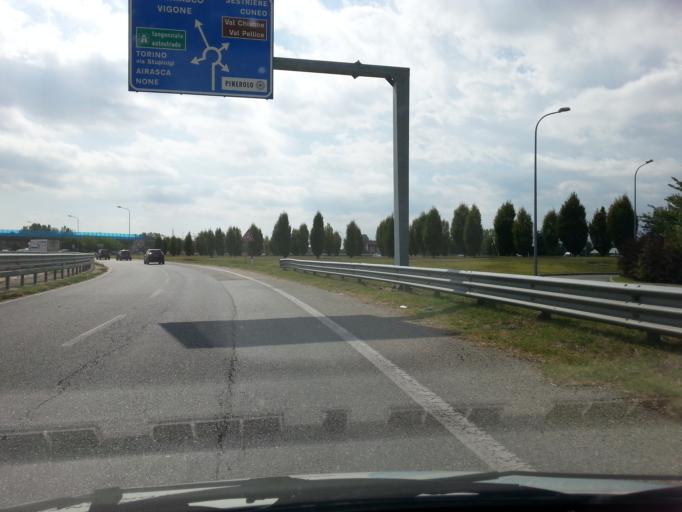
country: IT
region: Piedmont
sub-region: Provincia di Torino
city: Pinerolo
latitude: 44.8823
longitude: 7.3547
